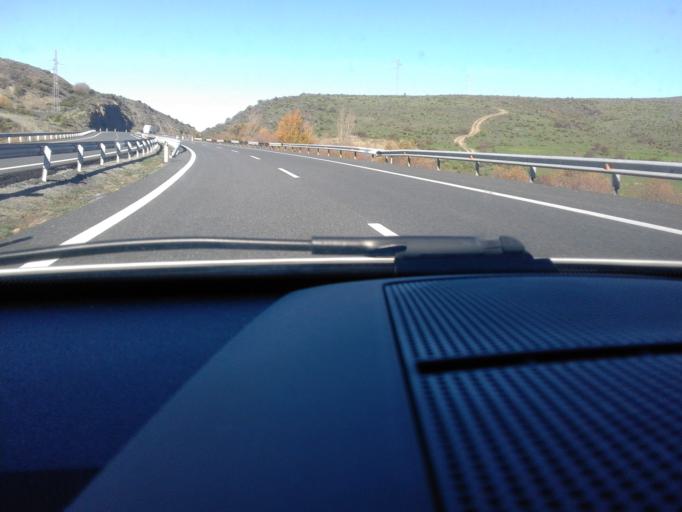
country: ES
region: Castille and Leon
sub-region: Provincia de Leon
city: Carrocera
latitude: 42.7509
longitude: -5.7705
